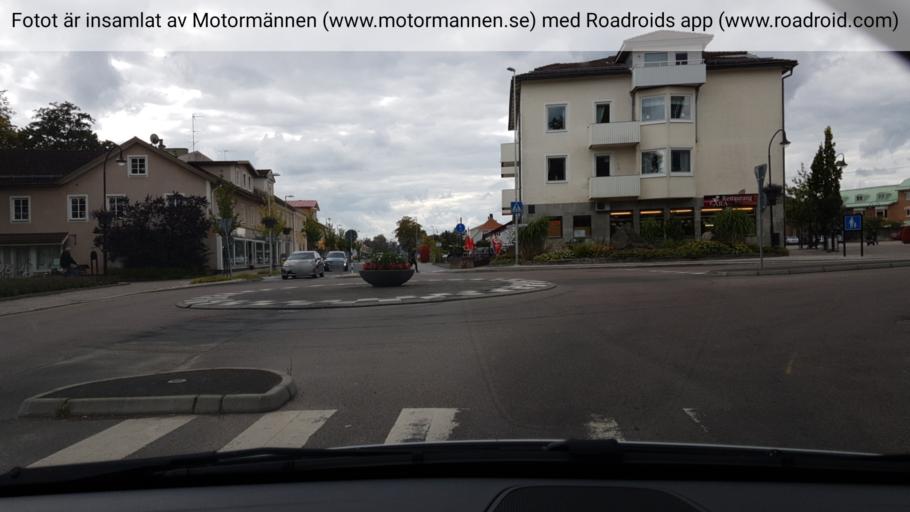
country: SE
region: Vaestra Goetaland
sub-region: Tidaholms Kommun
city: Tidaholm
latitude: 58.1804
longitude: 13.9598
